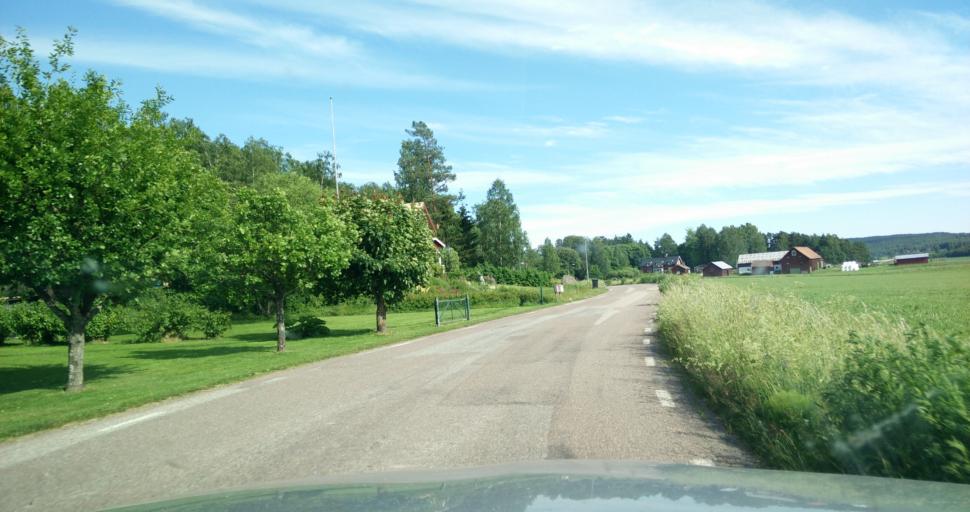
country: SE
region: Dalarna
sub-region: Hedemora Kommun
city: Langshyttan
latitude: 60.3867
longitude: 15.9838
